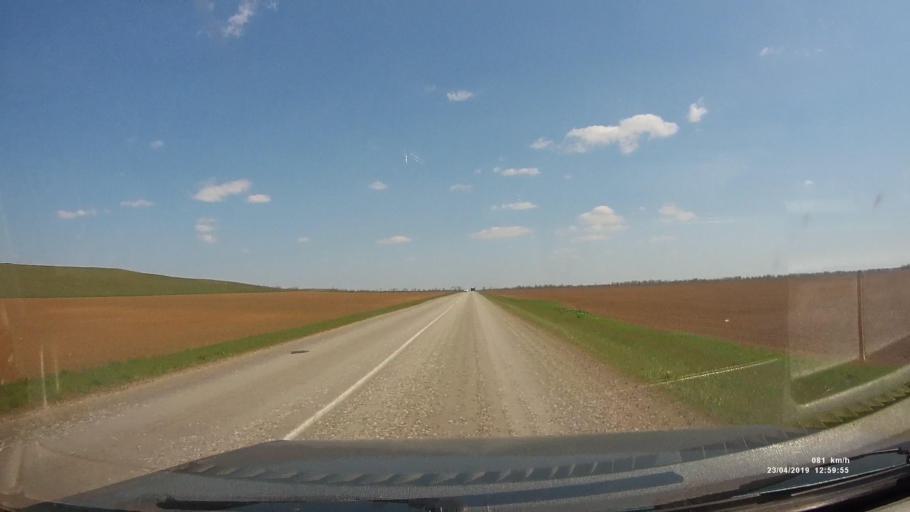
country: RU
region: Kalmykiya
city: Yashalta
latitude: 46.6042
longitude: 42.6253
